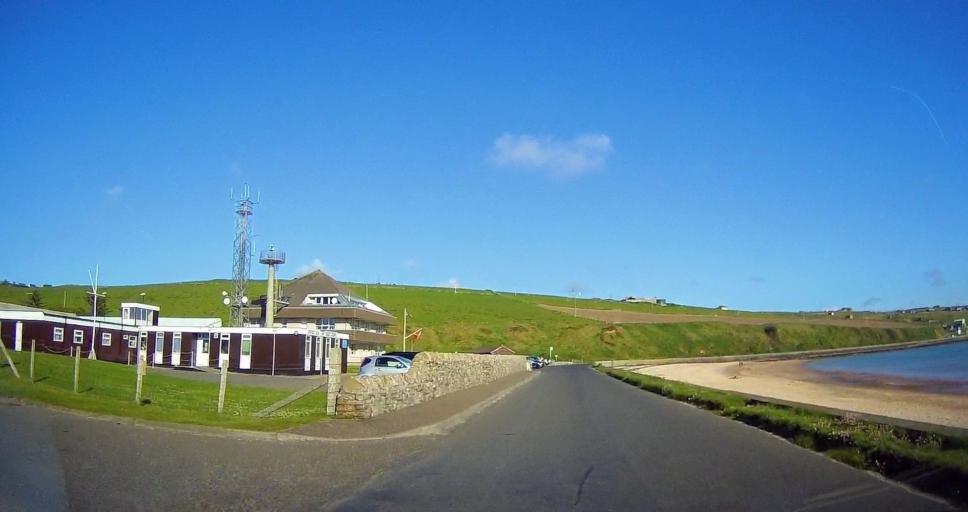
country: GB
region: Scotland
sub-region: Orkney Islands
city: Orkney
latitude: 58.9614
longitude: -2.9718
